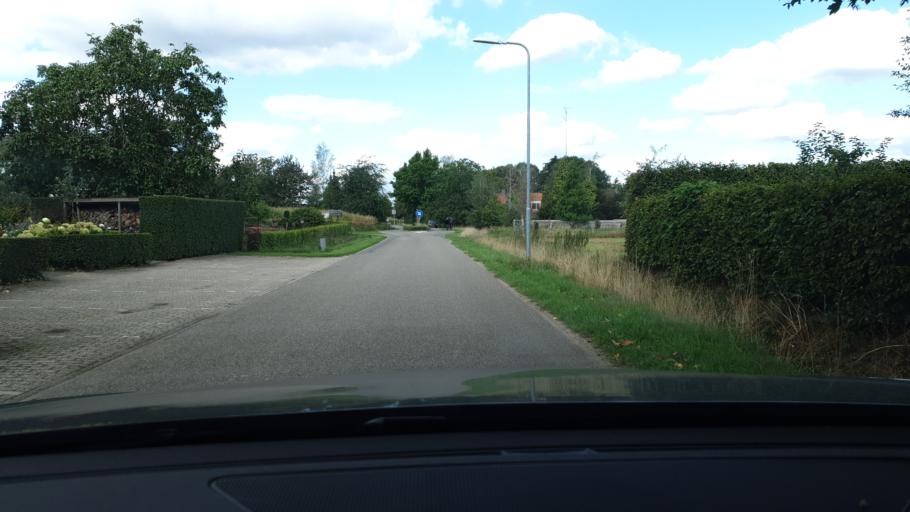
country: NL
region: Gelderland
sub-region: Gemeente Groesbeek
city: Bredeweg
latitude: 51.7535
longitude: 5.9514
